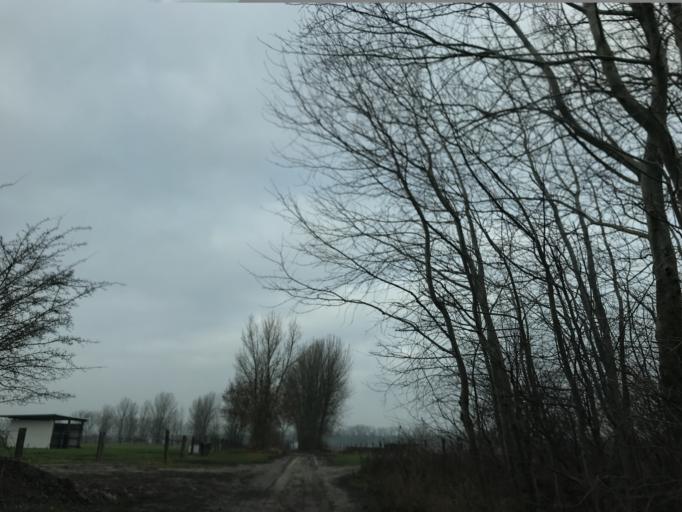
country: DE
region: Brandenburg
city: Kremmen
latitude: 52.7367
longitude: 12.9826
